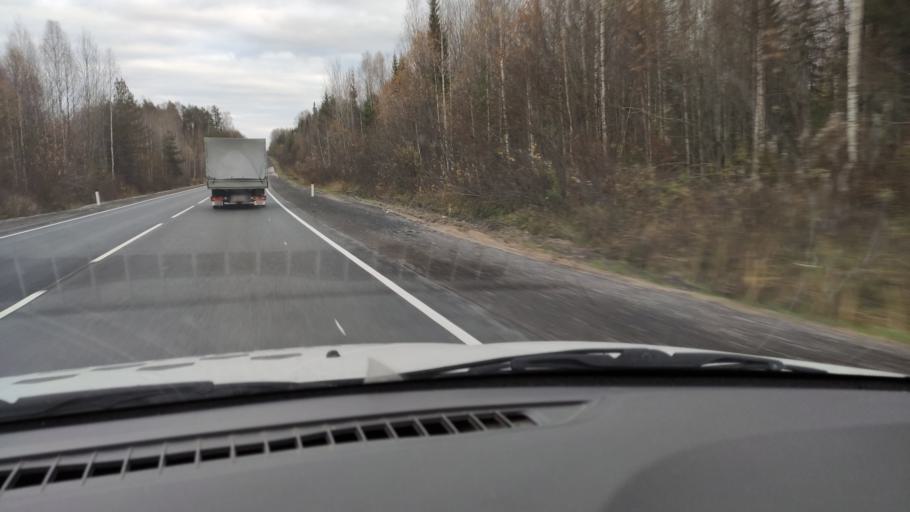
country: RU
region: Kirov
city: Chernaya Kholunitsa
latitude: 58.8725
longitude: 51.5209
